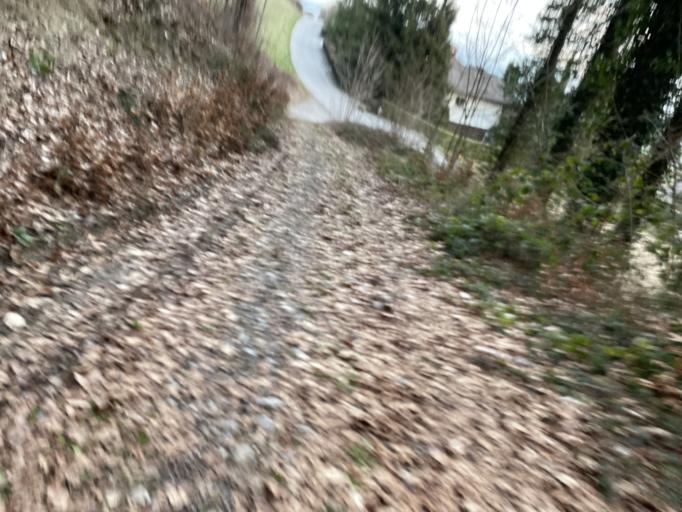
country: CH
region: Bern
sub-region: Bern-Mittelland District
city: Muhlethurnen
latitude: 46.8352
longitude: 7.5347
